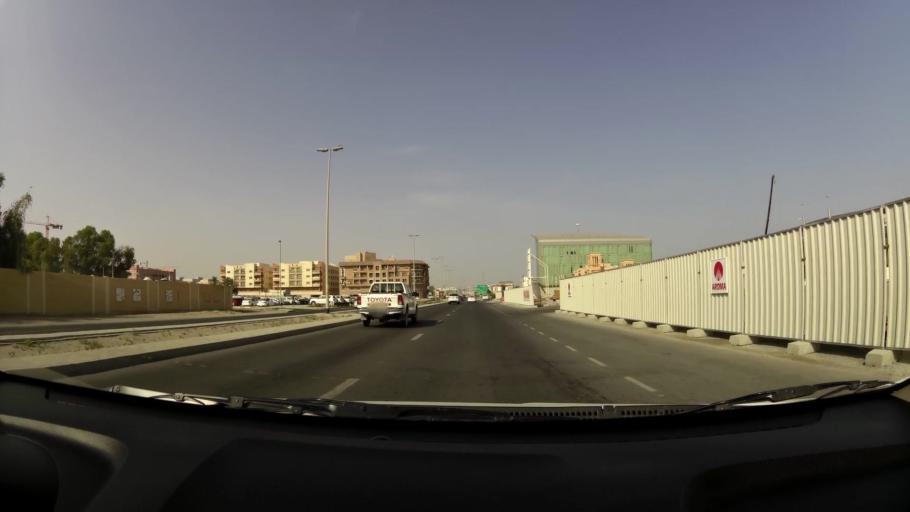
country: AE
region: Ash Shariqah
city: Sharjah
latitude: 25.2880
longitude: 55.3526
